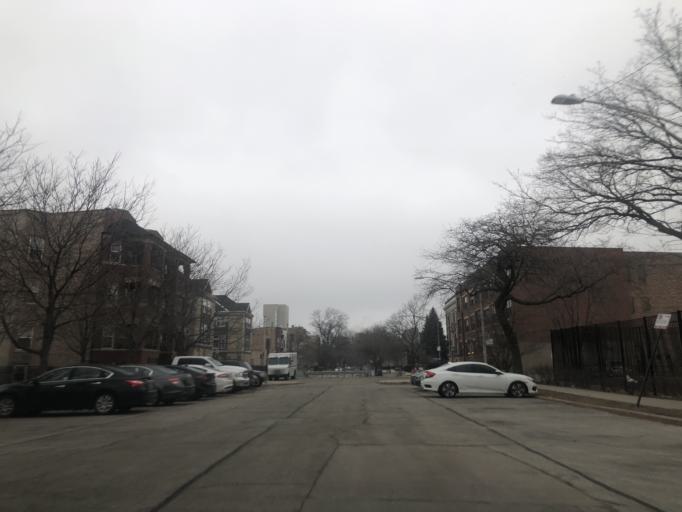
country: US
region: Illinois
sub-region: Cook County
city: Chicago
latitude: 41.7812
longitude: -87.6027
